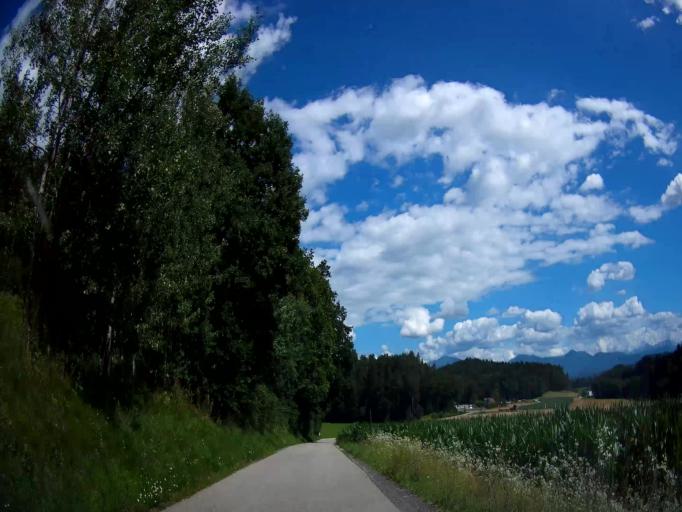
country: AT
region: Carinthia
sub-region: Politischer Bezirk Volkermarkt
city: Voelkermarkt
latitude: 46.6585
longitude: 14.5435
